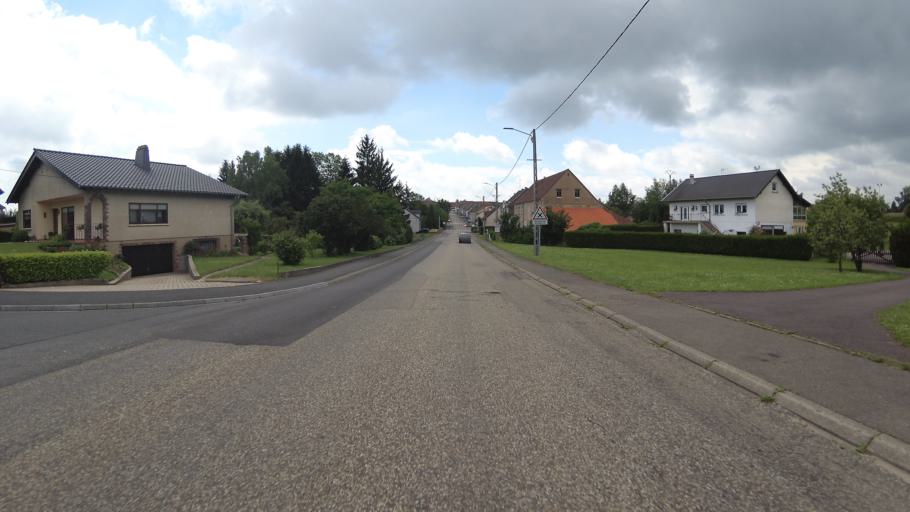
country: FR
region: Lorraine
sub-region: Departement de la Moselle
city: Remelfing
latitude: 49.0653
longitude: 7.0905
